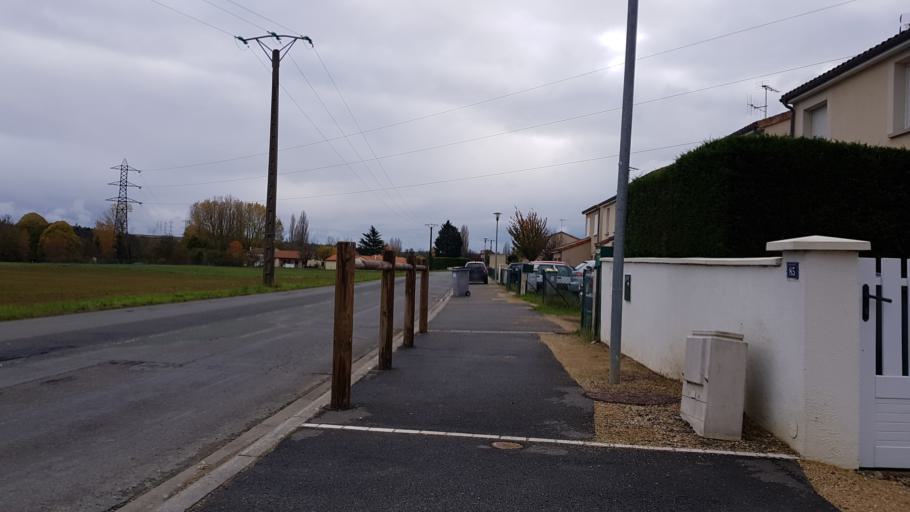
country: FR
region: Poitou-Charentes
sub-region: Departement de la Vienne
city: Chasseneuil-du-Poitou
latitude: 46.6608
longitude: 0.3811
